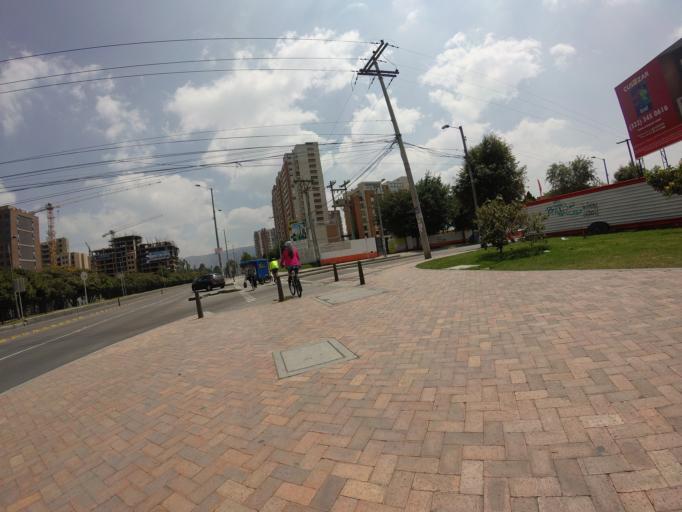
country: CO
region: Cundinamarca
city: Cota
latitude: 4.7398
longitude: -74.0576
